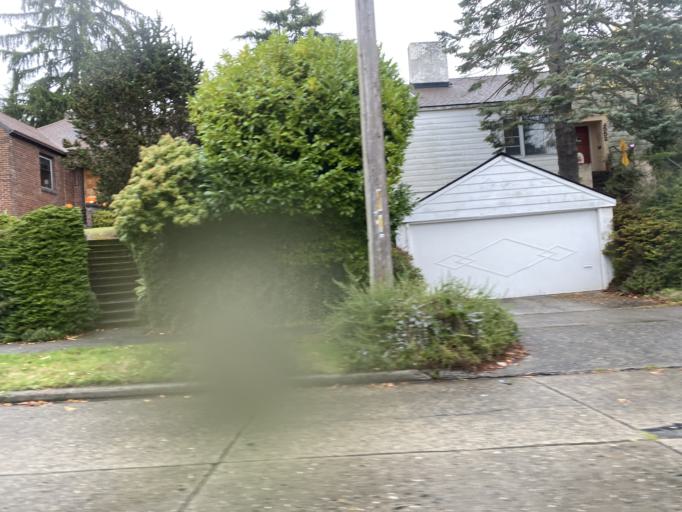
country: US
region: Washington
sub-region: King County
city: Seattle
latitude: 47.6427
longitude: -122.3930
